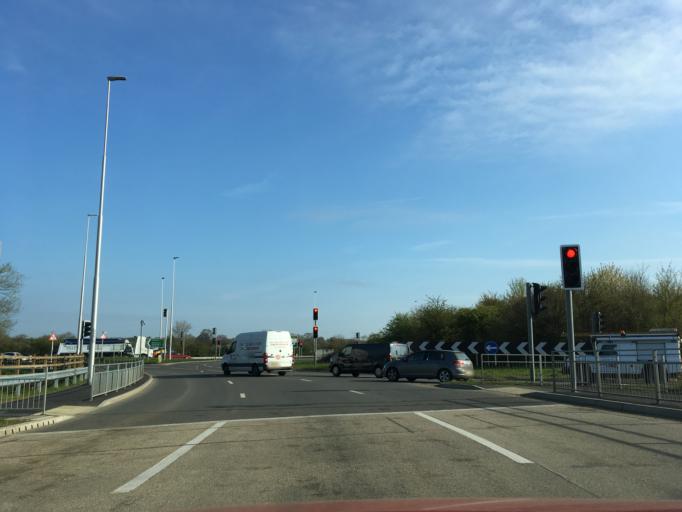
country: GB
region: England
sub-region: Milton Keynes
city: Stony Stratford
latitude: 52.0659
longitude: -0.8708
